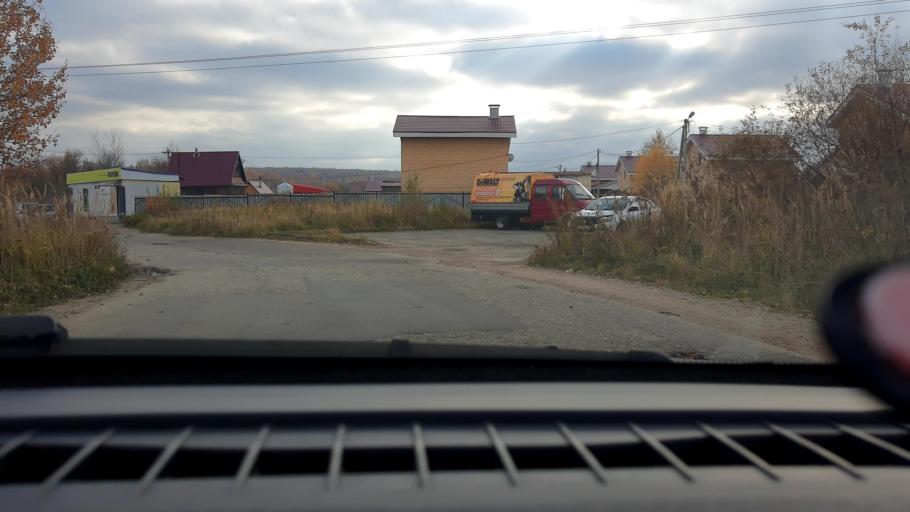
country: RU
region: Nizjnij Novgorod
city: Afonino
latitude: 56.1998
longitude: 44.0957
